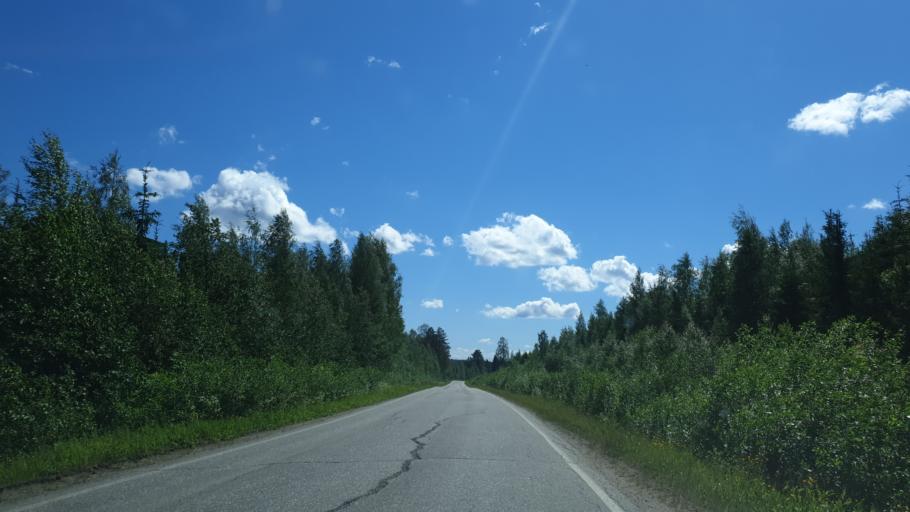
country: FI
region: Northern Savo
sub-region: Koillis-Savo
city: Kaavi
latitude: 62.9927
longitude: 28.5043
